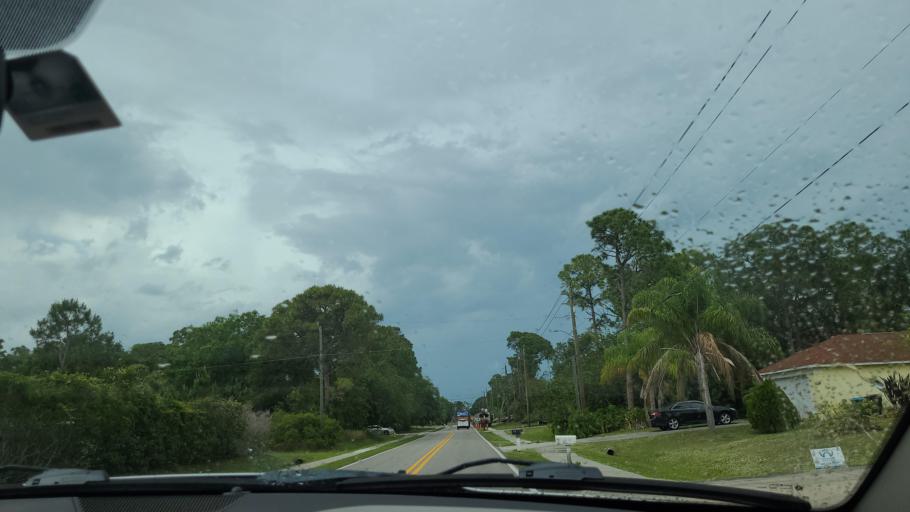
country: US
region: Florida
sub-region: Brevard County
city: Grant-Valkaria
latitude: 27.9532
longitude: -80.6420
